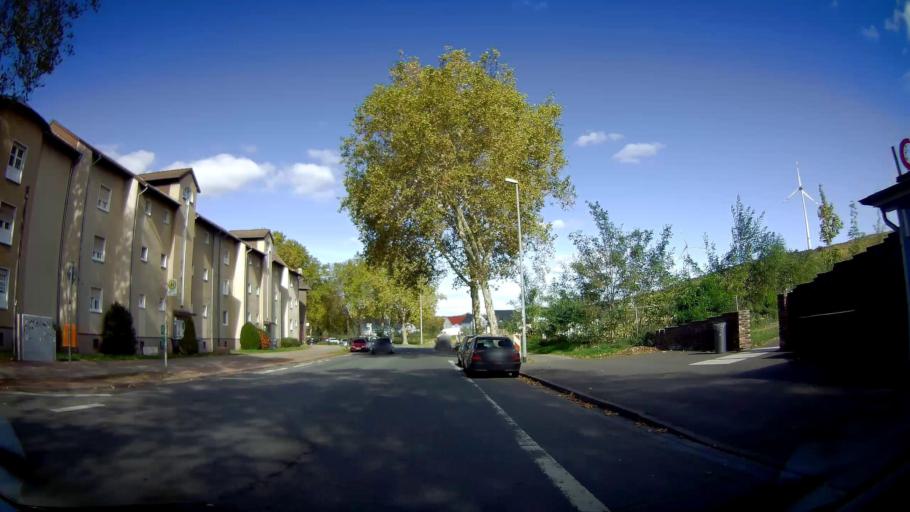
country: DE
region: North Rhine-Westphalia
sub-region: Regierungsbezirk Dusseldorf
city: Dinslaken
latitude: 51.5848
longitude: 6.7614
